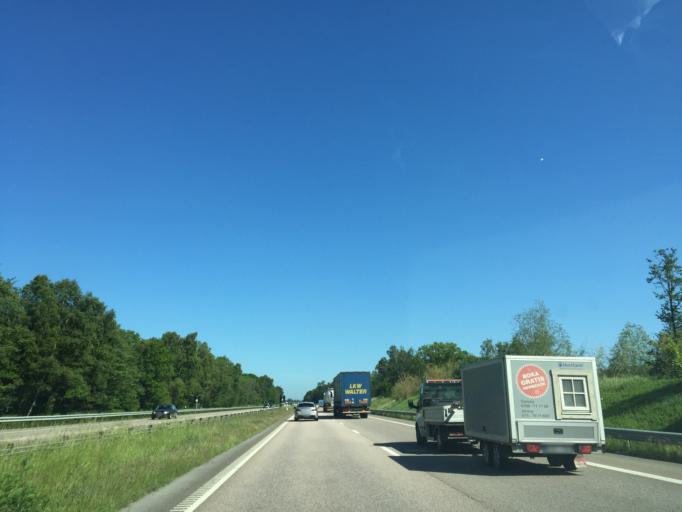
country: SE
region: Skane
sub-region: Helsingborg
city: Barslov
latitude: 56.0535
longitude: 12.7842
